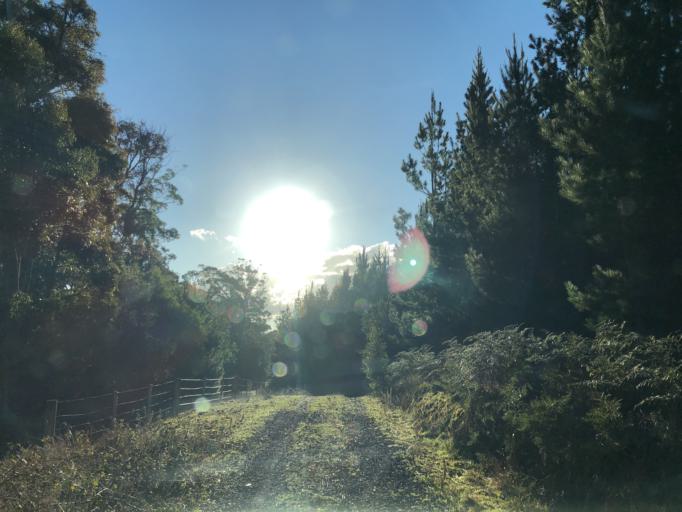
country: AU
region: Victoria
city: Brown Hill
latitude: -37.4934
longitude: 144.1421
